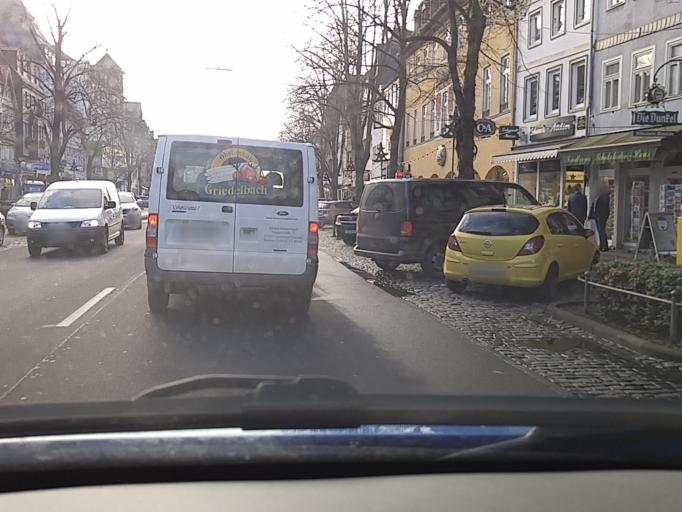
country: DE
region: Hesse
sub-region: Regierungsbezirk Darmstadt
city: Friedberg
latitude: 50.3378
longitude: 8.7539
